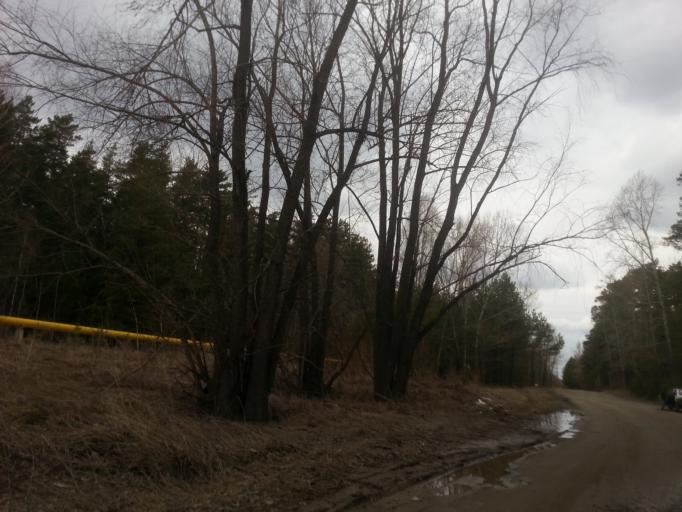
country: RU
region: Altai Krai
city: Yuzhnyy
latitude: 53.2798
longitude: 83.7352
